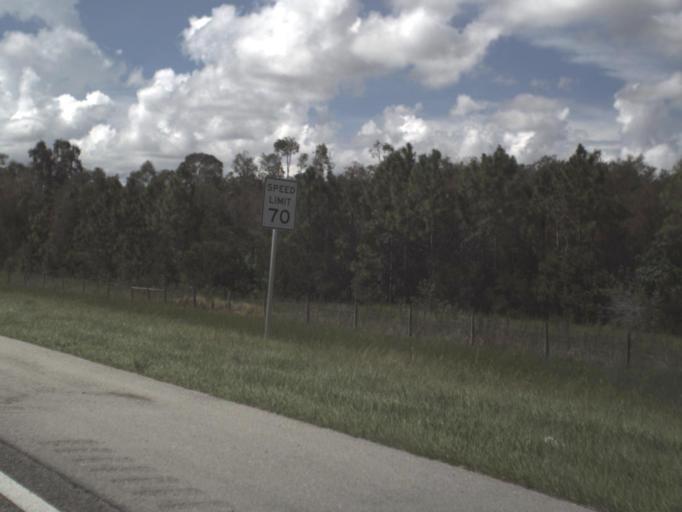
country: US
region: Florida
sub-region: Lee County
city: Fort Myers
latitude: 26.6227
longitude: -81.8059
